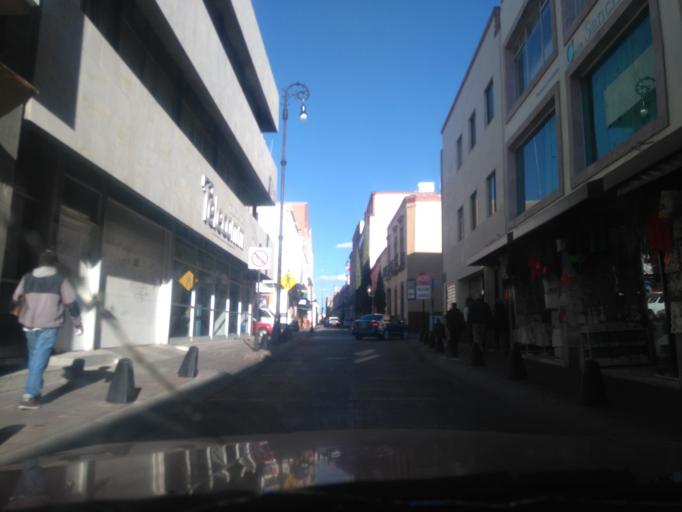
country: MX
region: Aguascalientes
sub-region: Aguascalientes
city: Aguascalientes
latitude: 21.8797
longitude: -102.2977
